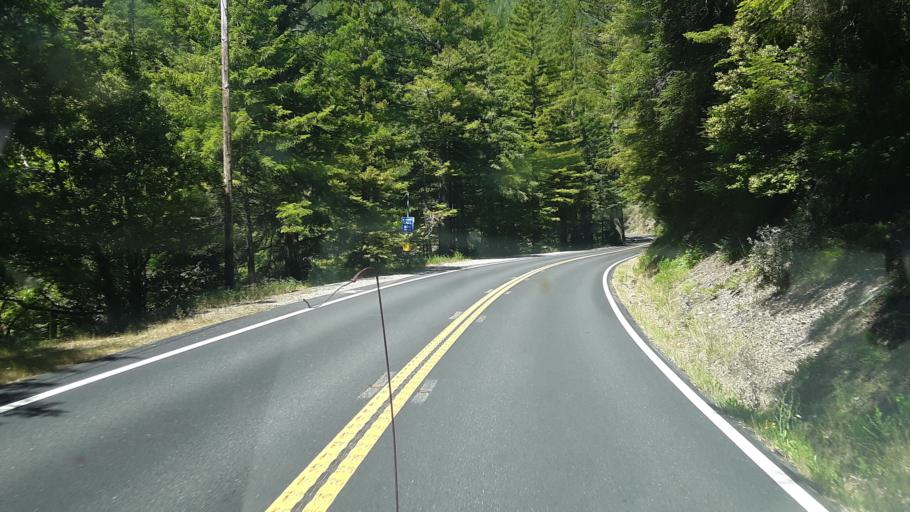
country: US
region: California
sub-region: Del Norte County
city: Bertsch-Oceanview
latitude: 41.8389
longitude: -124.0308
